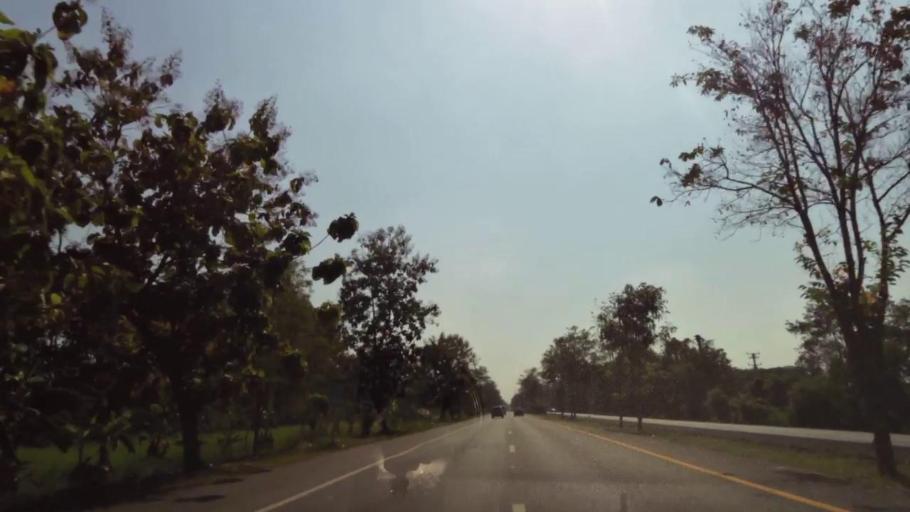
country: TH
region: Phichit
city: Bueng Na Rang
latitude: 16.0766
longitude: 100.1242
